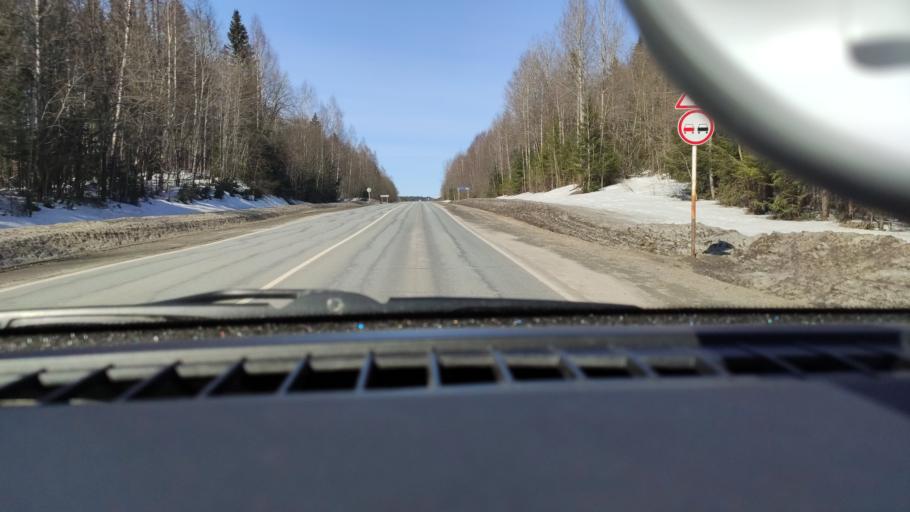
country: RU
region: Perm
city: Perm
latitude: 58.1501
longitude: 56.2576
